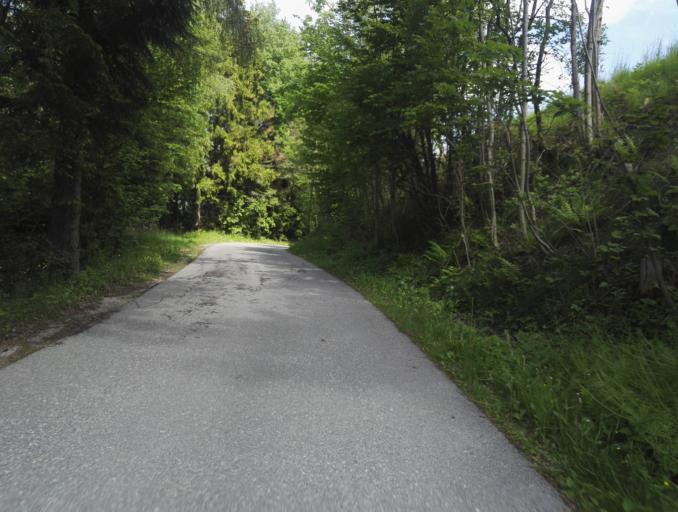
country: AT
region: Styria
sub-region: Politischer Bezirk Graz-Umgebung
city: Sankt Radegund bei Graz
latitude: 47.2088
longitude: 15.4569
